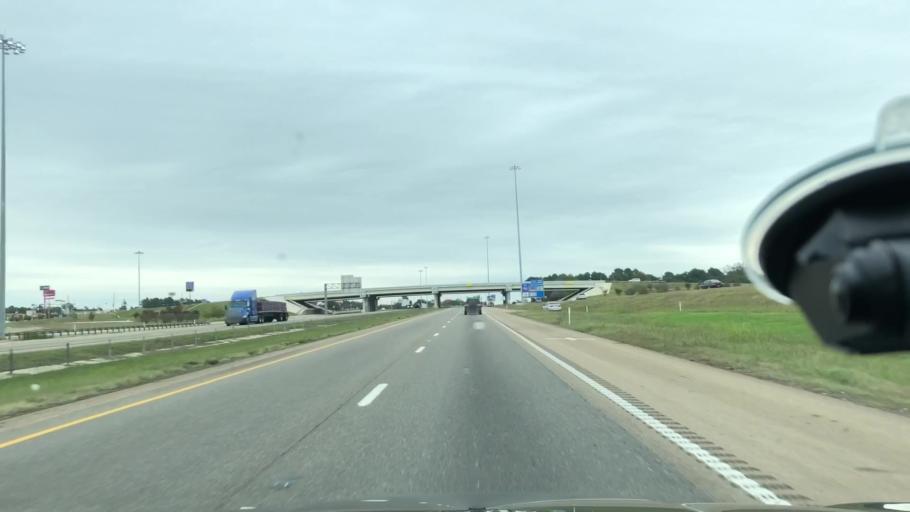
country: US
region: Arkansas
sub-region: Miller County
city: Texarkana
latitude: 33.4636
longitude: -94.0699
